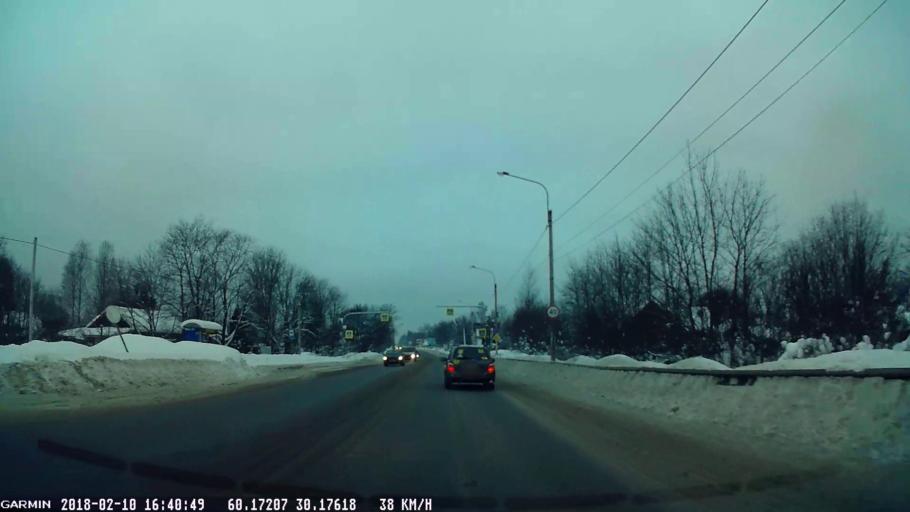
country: RU
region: Leningrad
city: Sertolovo
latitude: 60.1620
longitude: 30.1836
